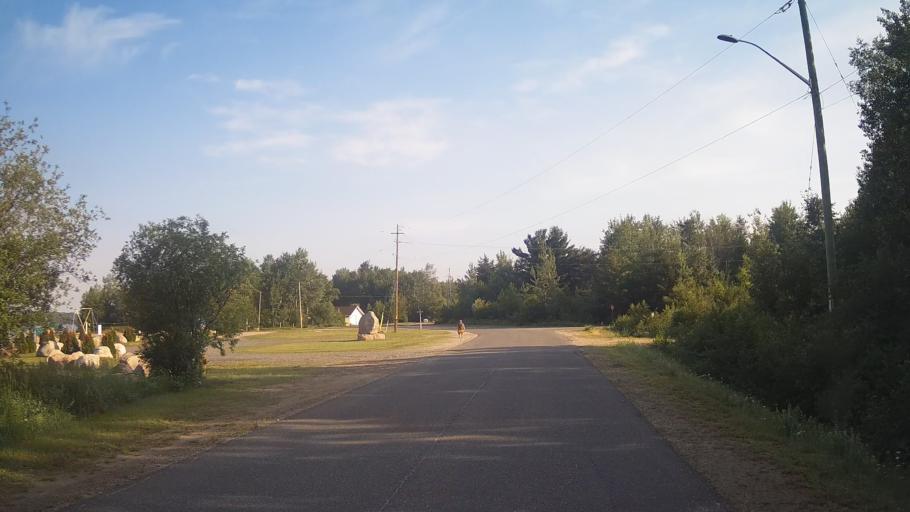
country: CA
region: Ontario
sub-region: Rainy River District
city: Atikokan
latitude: 49.4040
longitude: -91.6664
